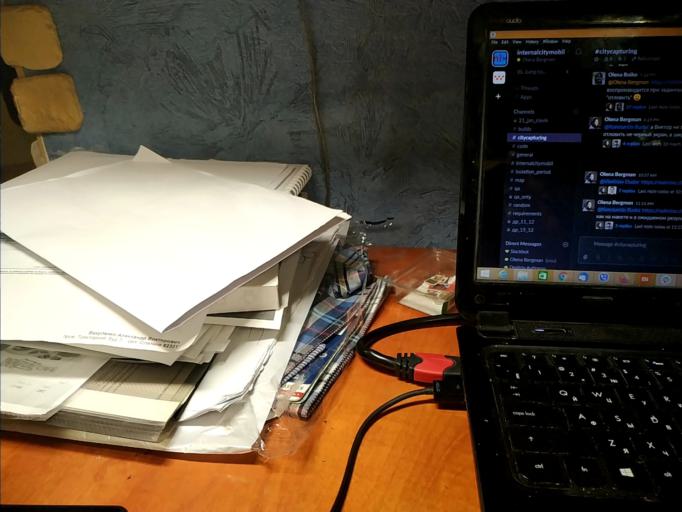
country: RU
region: Vologda
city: Suda
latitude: 58.8446
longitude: 37.5434
